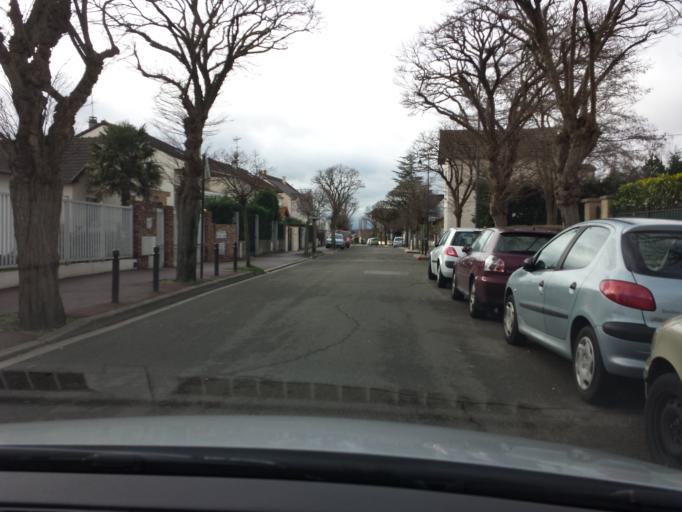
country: FR
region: Ile-de-France
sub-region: Departement des Hauts-de-Seine
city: Antony
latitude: 48.7501
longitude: 2.2880
